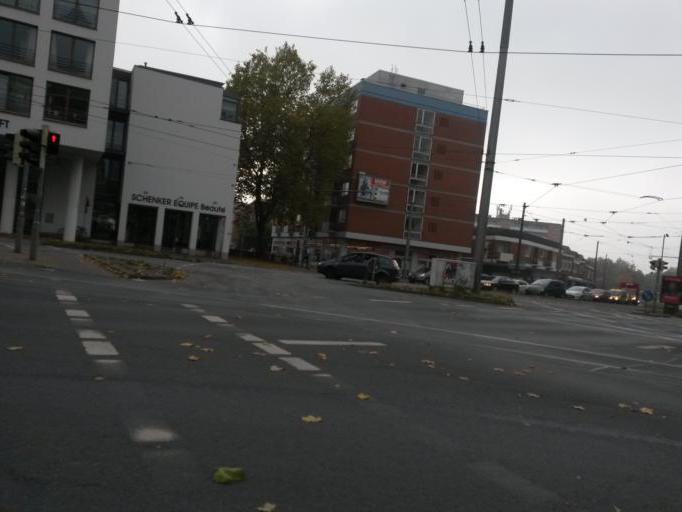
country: DE
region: Bremen
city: Bremen
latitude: 53.0717
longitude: 8.8015
